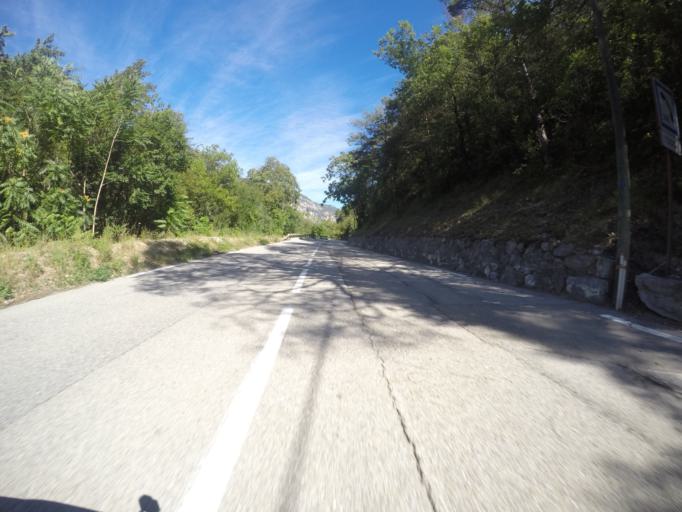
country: FR
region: Provence-Alpes-Cote d'Azur
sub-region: Departement des Alpes-Maritimes
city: Gilette
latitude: 43.9581
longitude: 7.1568
